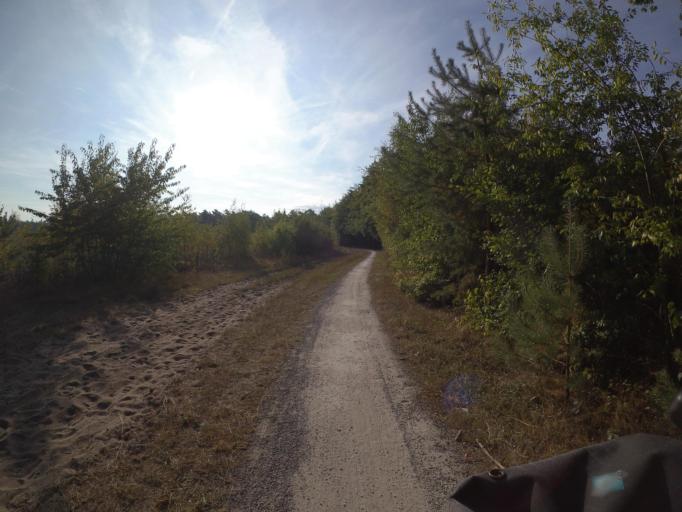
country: NL
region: Drenthe
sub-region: Gemeente Westerveld
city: Dwingeloo
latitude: 52.9225
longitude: 6.3270
